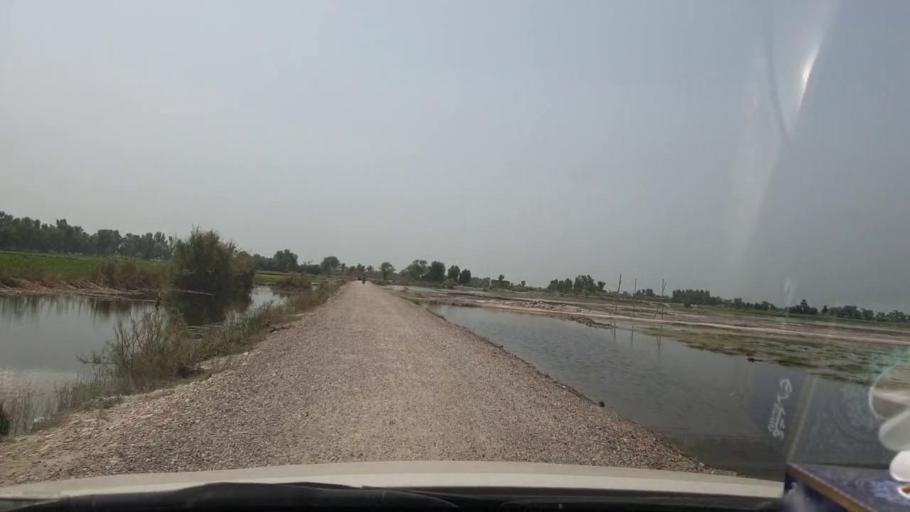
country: PK
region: Sindh
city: Shikarpur
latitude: 27.9866
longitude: 68.7064
